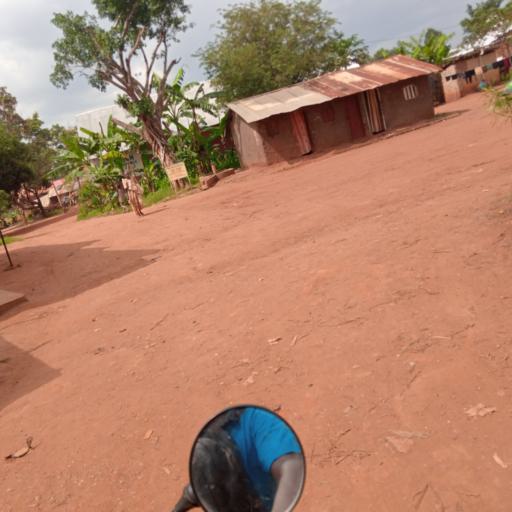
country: UG
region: Eastern Region
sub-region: Mbale District
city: Mbale
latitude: 1.1027
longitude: 34.1822
